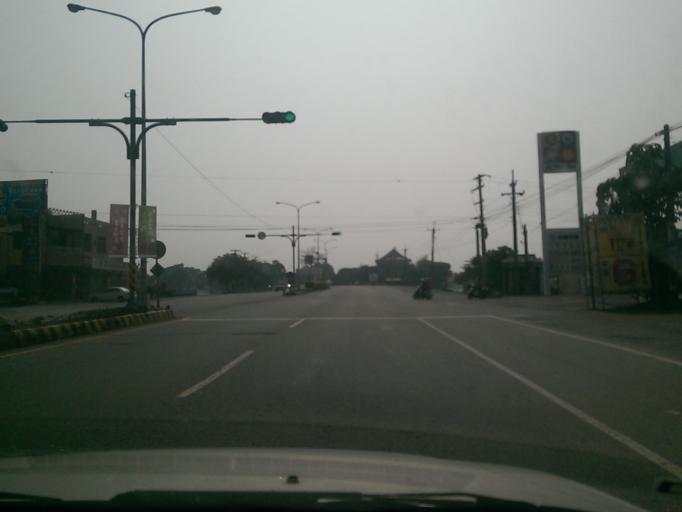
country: TW
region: Taiwan
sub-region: Yunlin
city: Douliu
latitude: 23.7740
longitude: 120.4794
